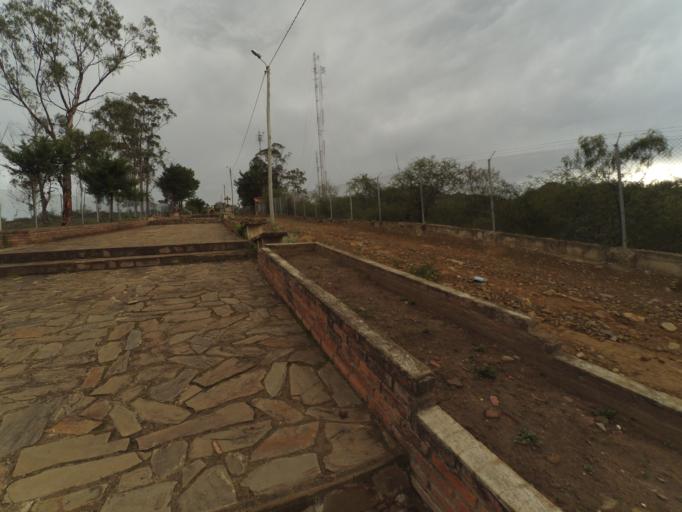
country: BO
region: Chuquisaca
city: Padilla
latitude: -19.3144
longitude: -64.3081
